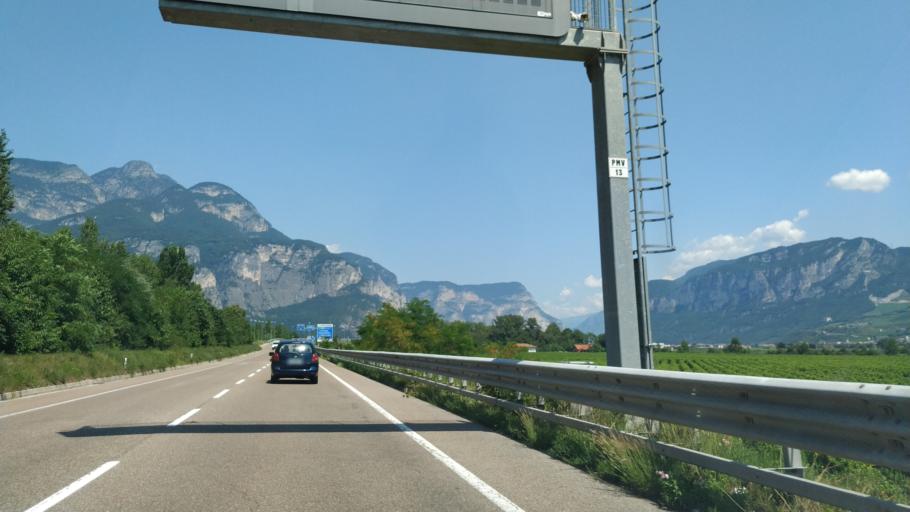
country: IT
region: Trentino-Alto Adige
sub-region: Provincia di Trento
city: Nave San Rocco
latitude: 46.1840
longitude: 11.0975
